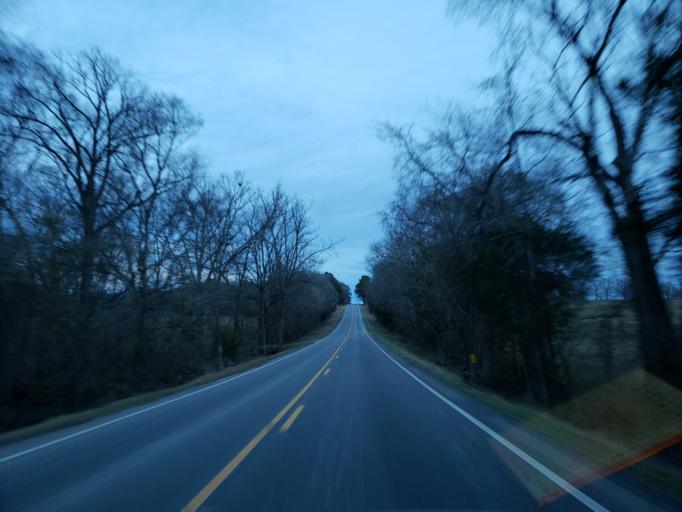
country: US
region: Alabama
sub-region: Sumter County
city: Livingston
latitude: 32.8112
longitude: -88.2590
